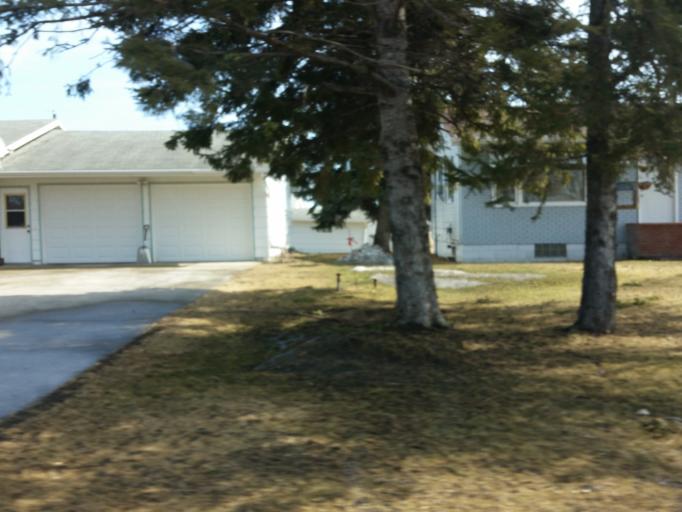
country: US
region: North Dakota
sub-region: Walsh County
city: Grafton
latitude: 48.2938
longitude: -97.2547
